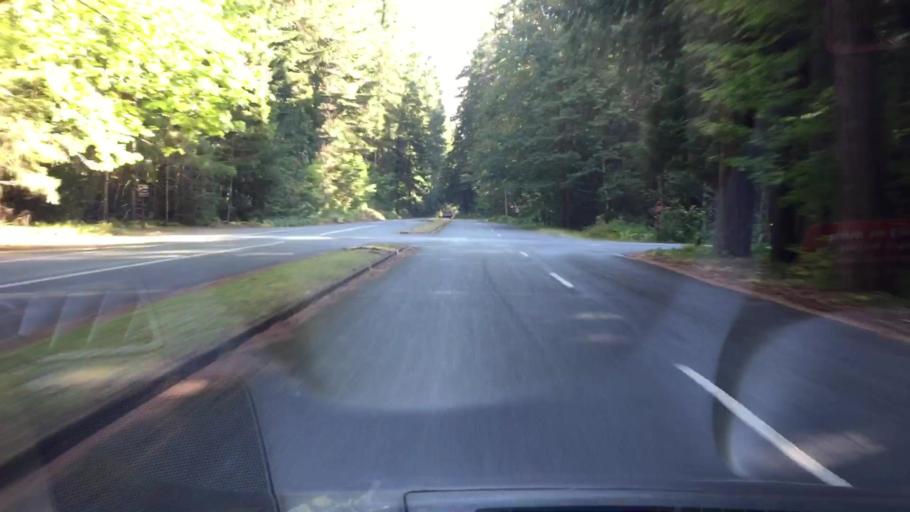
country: US
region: Washington
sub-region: Pierce County
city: Buckley
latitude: 46.7327
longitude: -121.5686
